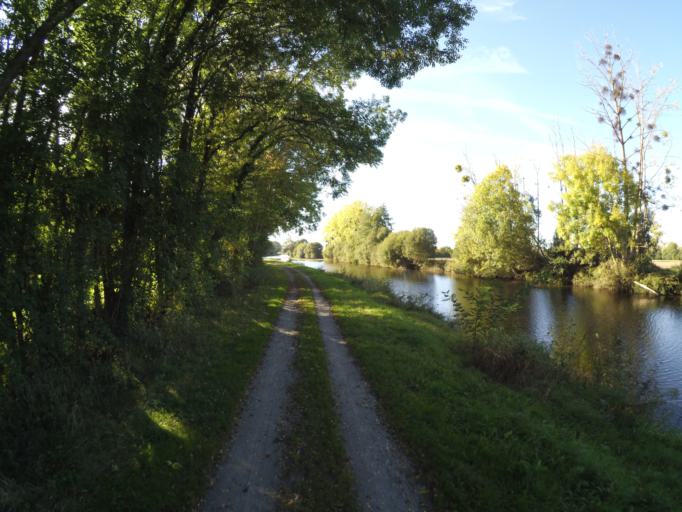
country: FR
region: Brittany
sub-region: Departement du Morbihan
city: Peillac
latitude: 47.7235
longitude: -2.1926
